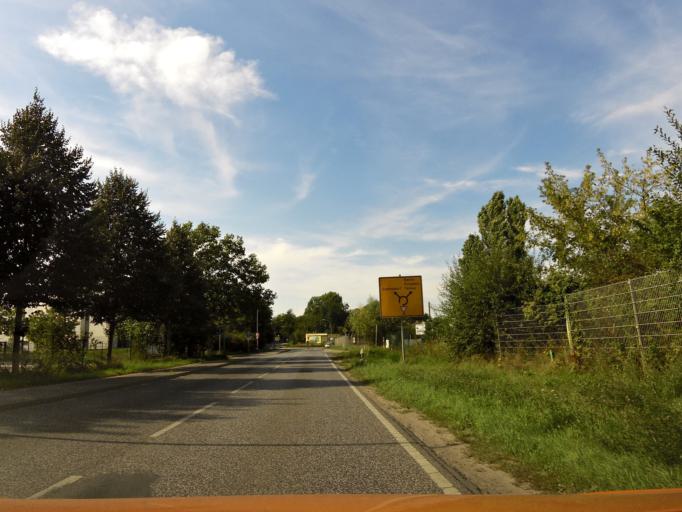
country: DE
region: Brandenburg
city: Teltow
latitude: 52.3805
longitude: 13.2498
